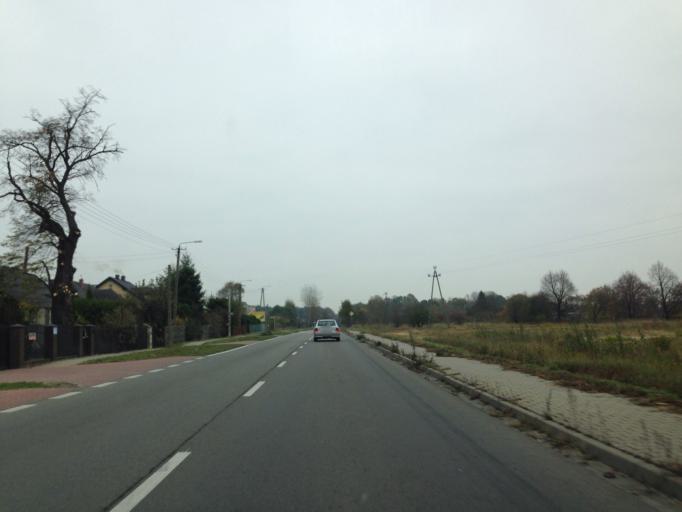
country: PL
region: Masovian Voivodeship
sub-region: Powiat warszawski zachodni
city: Leszno
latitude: 52.2626
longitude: 20.6416
